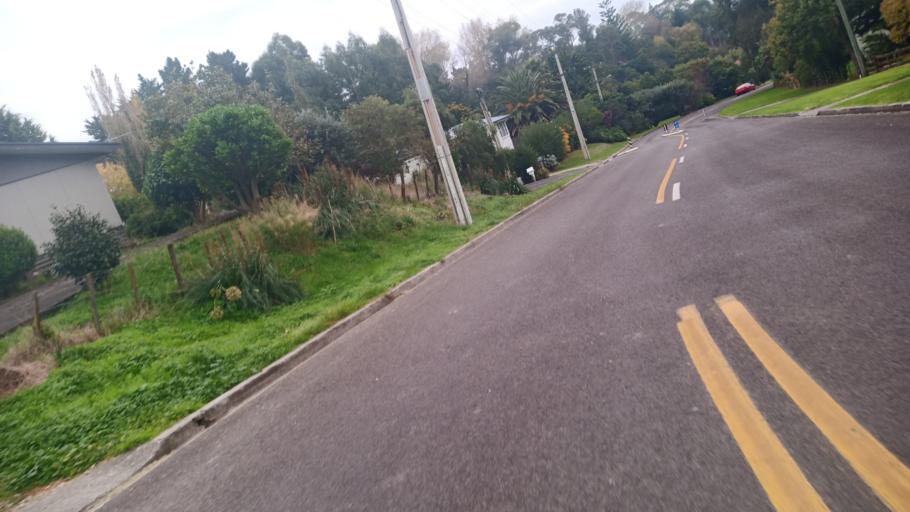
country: NZ
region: Gisborne
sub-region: Gisborne District
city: Gisborne
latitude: -38.6814
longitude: 178.0394
